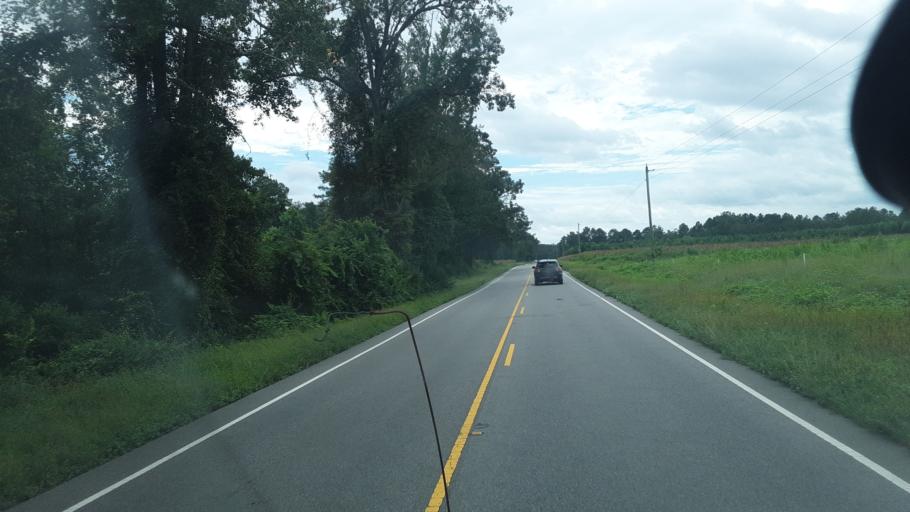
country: US
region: North Carolina
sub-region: Robeson County
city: Rowland
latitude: 34.6126
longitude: -79.3328
